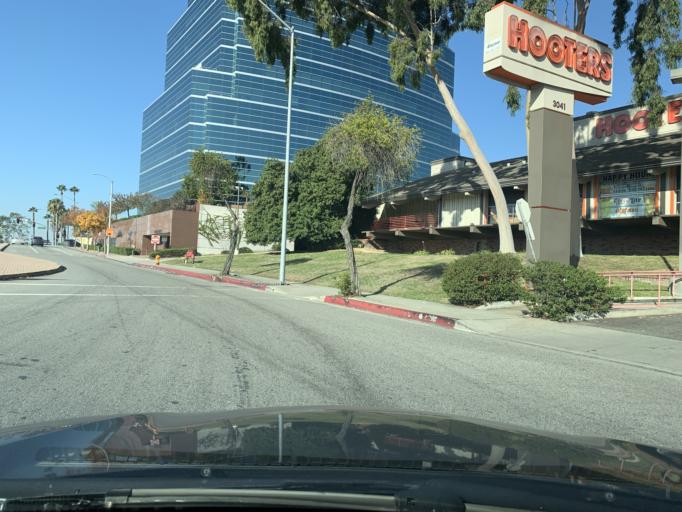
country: US
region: California
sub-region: Los Angeles County
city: Covina
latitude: 34.0726
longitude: -117.8798
